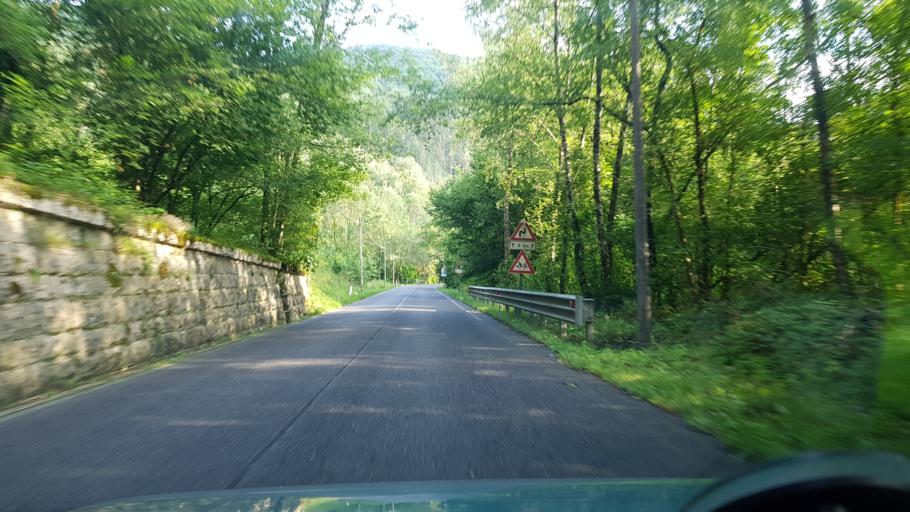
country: IT
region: Friuli Venezia Giulia
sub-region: Provincia di Udine
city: Lusevera
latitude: 46.2597
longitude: 13.2574
